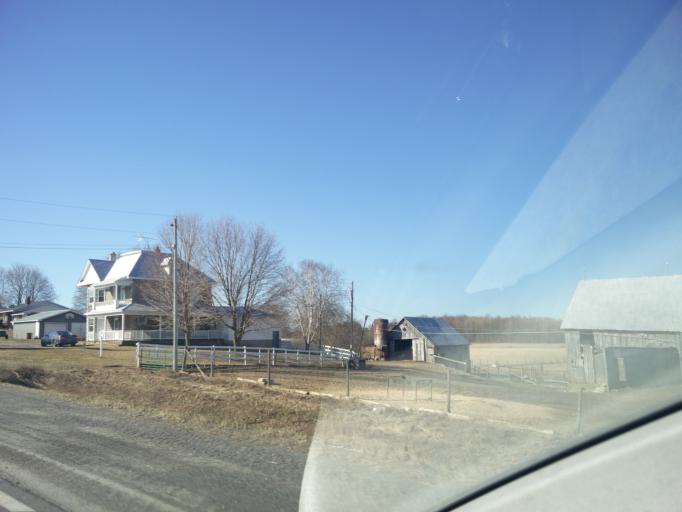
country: CA
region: Ontario
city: Bells Corners
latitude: 45.1710
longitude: -75.7148
